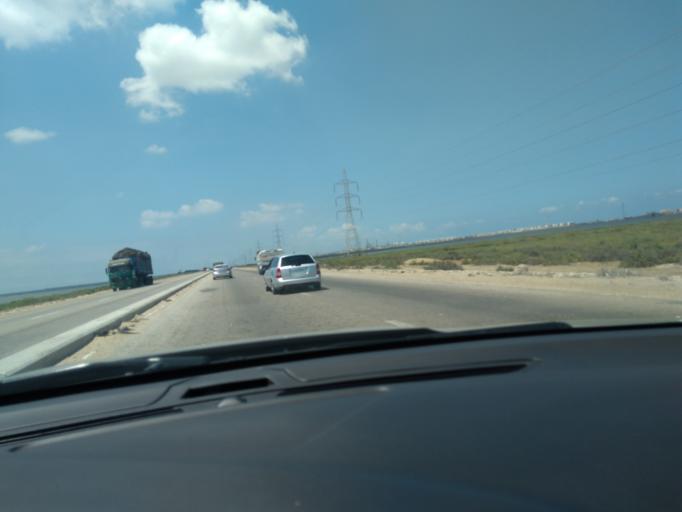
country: EG
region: Muhafazat Bur Sa`id
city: Port Said
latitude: 31.2780
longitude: 32.1961
